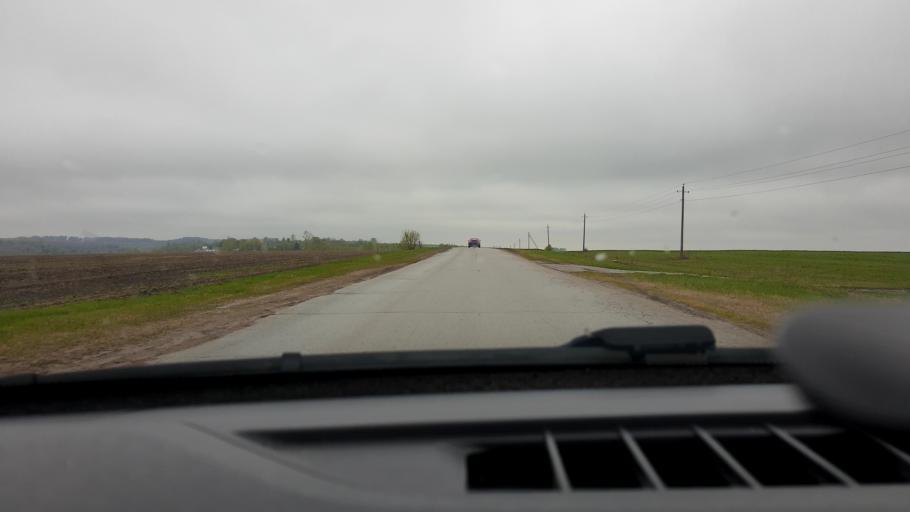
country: RU
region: Nizjnij Novgorod
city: Dal'neye Konstantinovo
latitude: 55.7637
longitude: 44.2432
